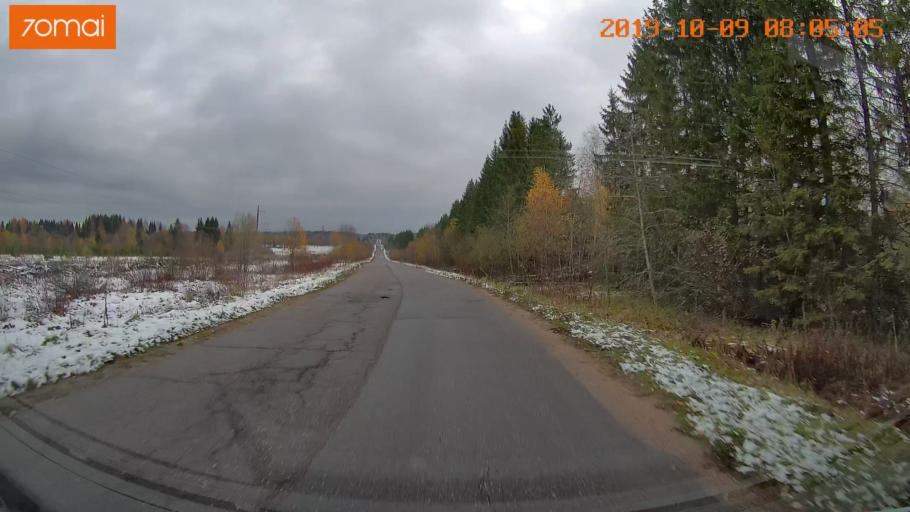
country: RU
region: Jaroslavl
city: Kukoboy
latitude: 58.6906
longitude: 40.0376
